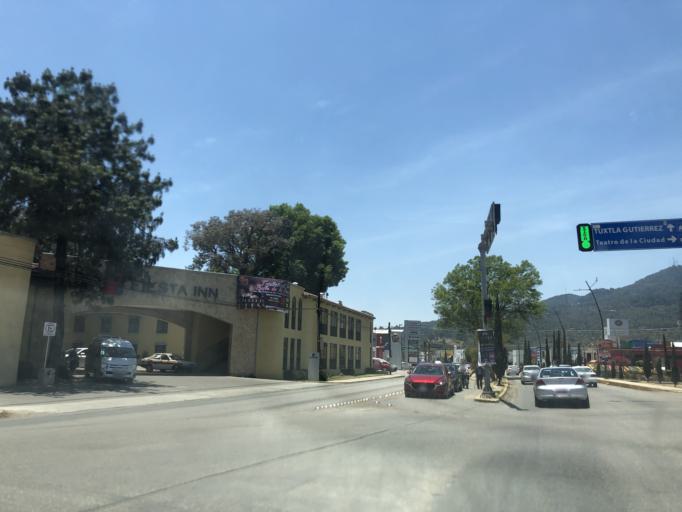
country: MX
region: Chiapas
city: San Cristobal de las Casas
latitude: 16.7324
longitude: -92.6523
